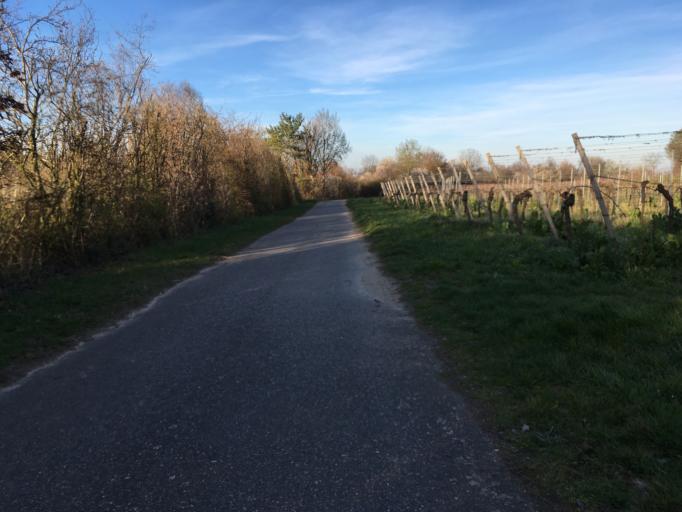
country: DE
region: Rheinland-Pfalz
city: Deidesheim
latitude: 49.3801
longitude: 8.1618
